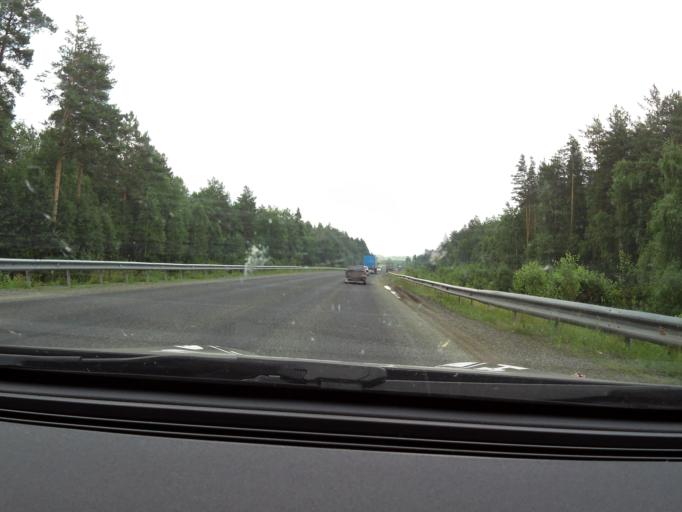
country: RU
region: Sverdlovsk
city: Ufimskiy
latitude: 56.7675
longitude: 58.1769
